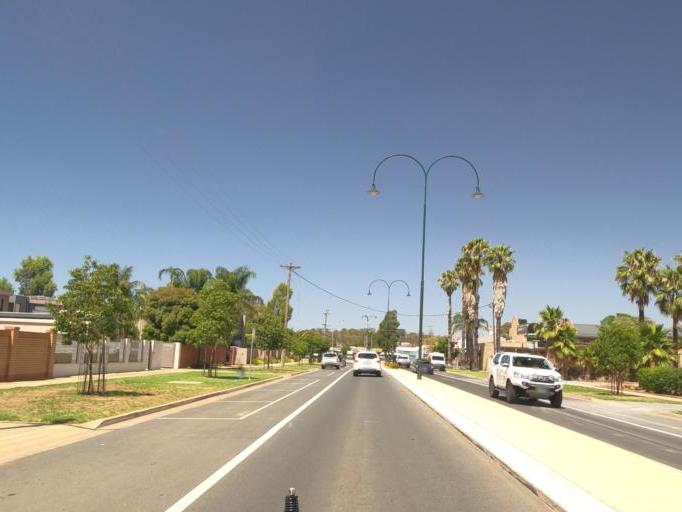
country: AU
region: New South Wales
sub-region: Corowa Shire
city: Mulwala
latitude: -35.9913
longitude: 146.0034
